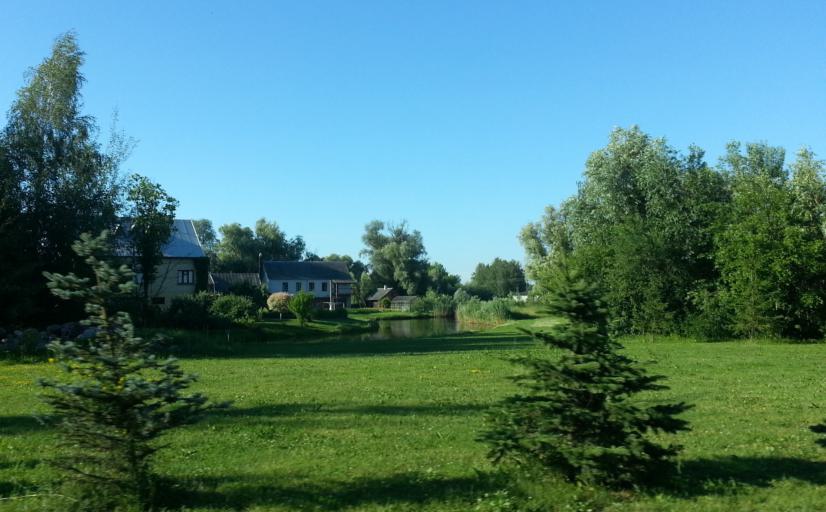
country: LT
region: Panevezys
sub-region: Birzai
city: Birzai
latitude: 56.2043
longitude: 24.7285
